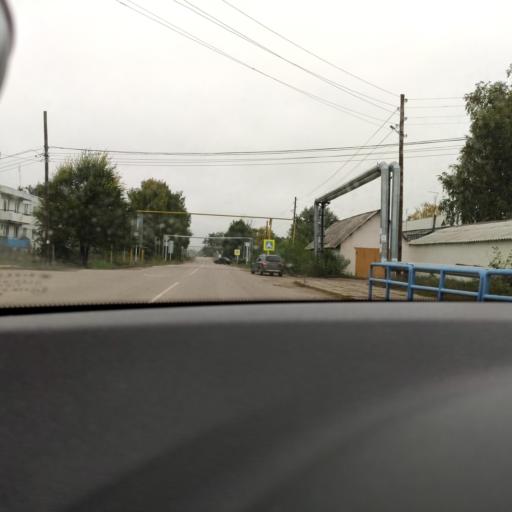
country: RU
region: Samara
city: Yelkhovka
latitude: 53.7370
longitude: 50.3162
